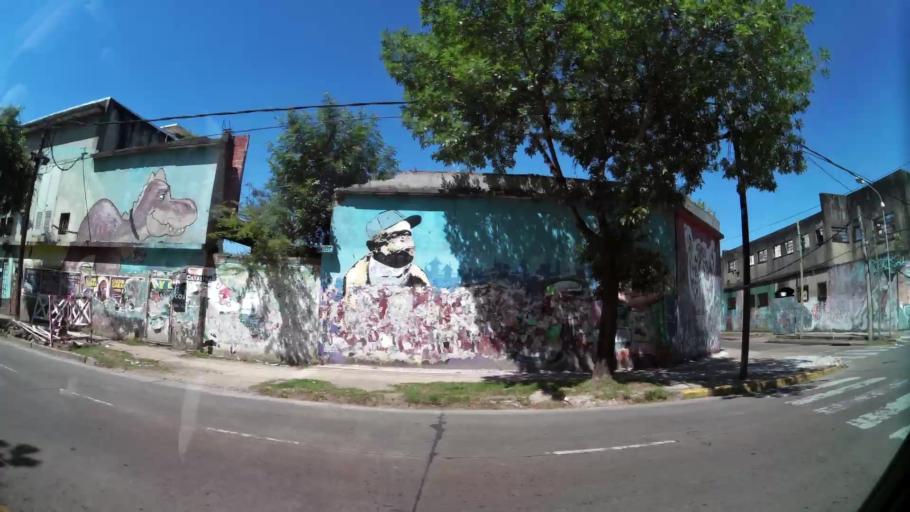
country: AR
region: Buenos Aires
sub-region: Partido de Tigre
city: Tigre
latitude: -34.4297
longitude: -58.5643
